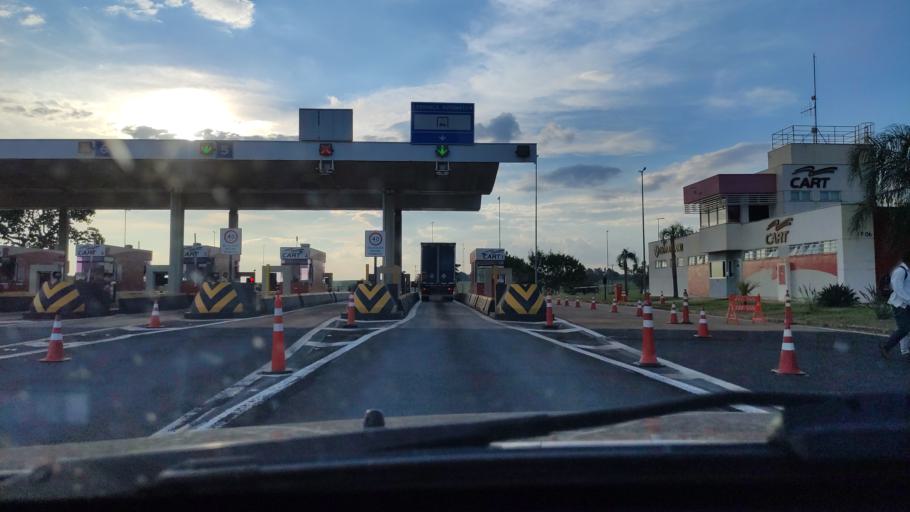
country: BR
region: Sao Paulo
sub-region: Rancharia
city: Rancharia
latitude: -22.4352
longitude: -51.0078
